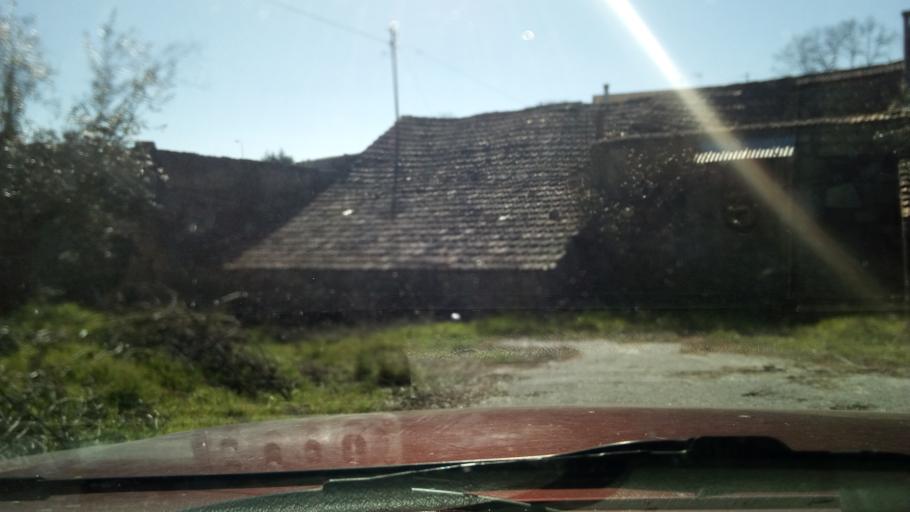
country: PT
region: Guarda
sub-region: Fornos de Algodres
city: Fornos de Algodres
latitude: 40.6149
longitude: -7.5354
